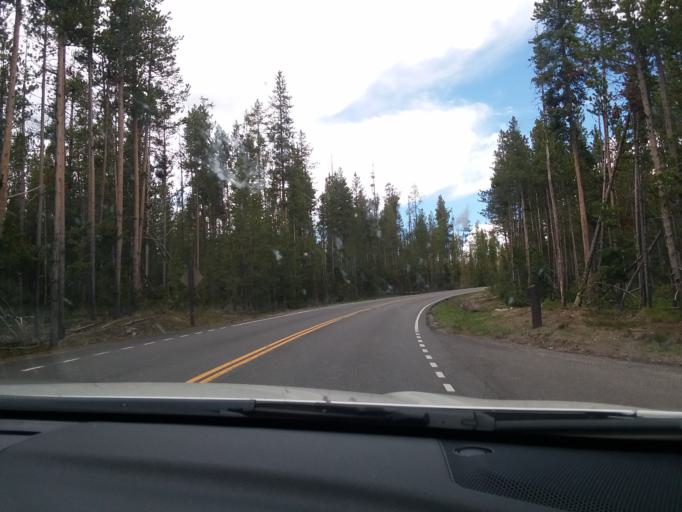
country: US
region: Idaho
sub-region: Teton County
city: Driggs
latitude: 44.1523
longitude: -110.6739
